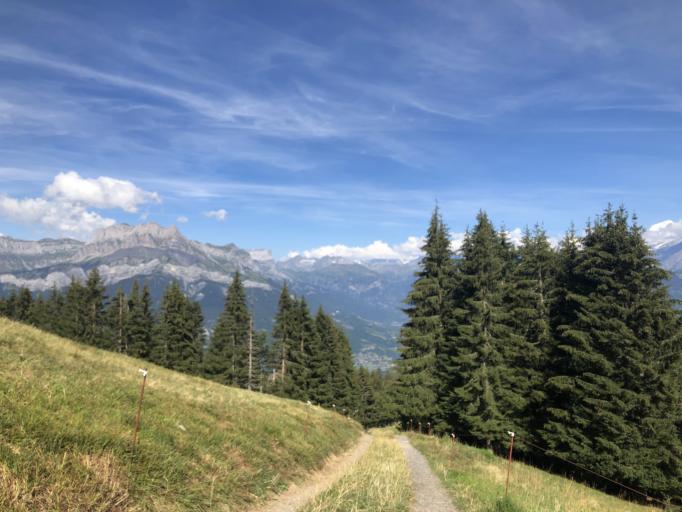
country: FR
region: Rhone-Alpes
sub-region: Departement de la Haute-Savoie
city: Cordon
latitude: 45.9103
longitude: 6.5778
